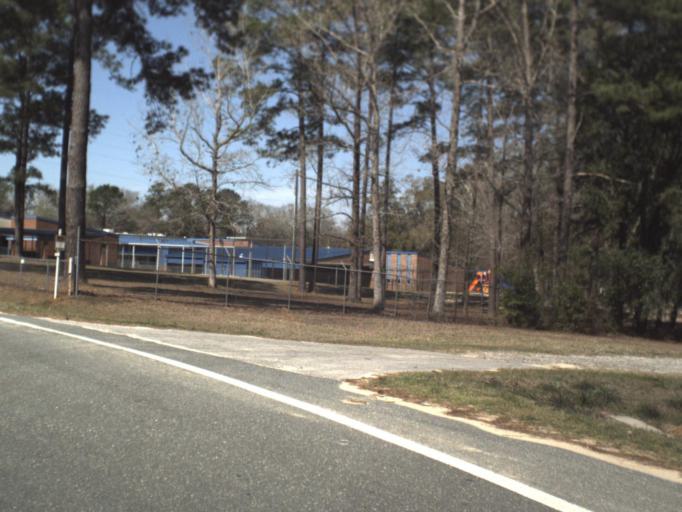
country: US
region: Florida
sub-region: Jackson County
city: Marianna
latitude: 30.7923
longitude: -85.3649
